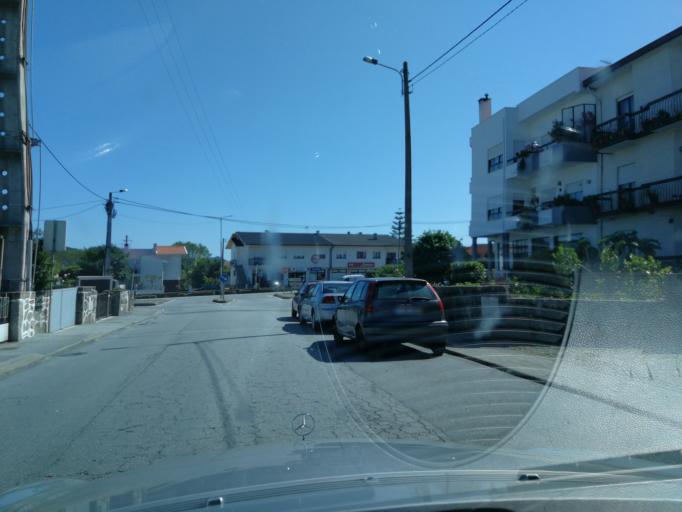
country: PT
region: Viana do Castelo
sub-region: Viana do Castelo
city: Meadela
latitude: 41.7073
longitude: -8.8035
